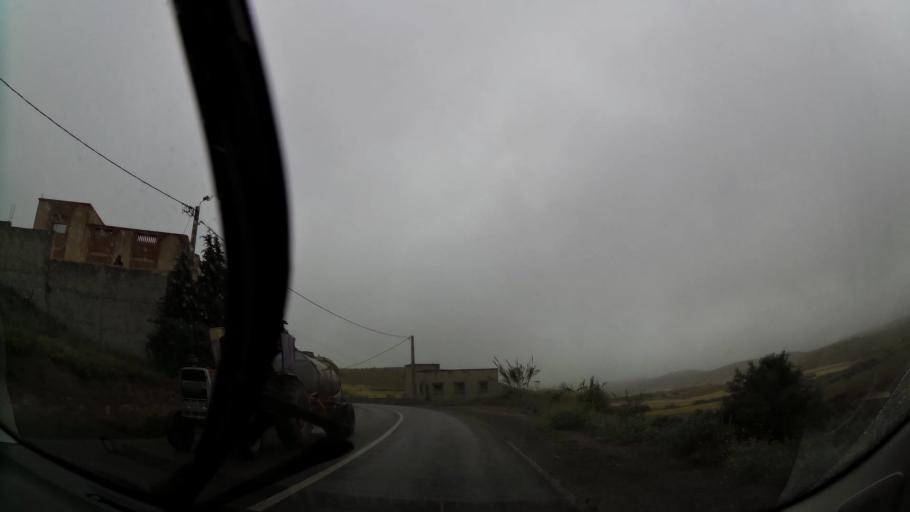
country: MA
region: Oriental
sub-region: Nador
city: Boudinar
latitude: 35.1290
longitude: -3.5827
